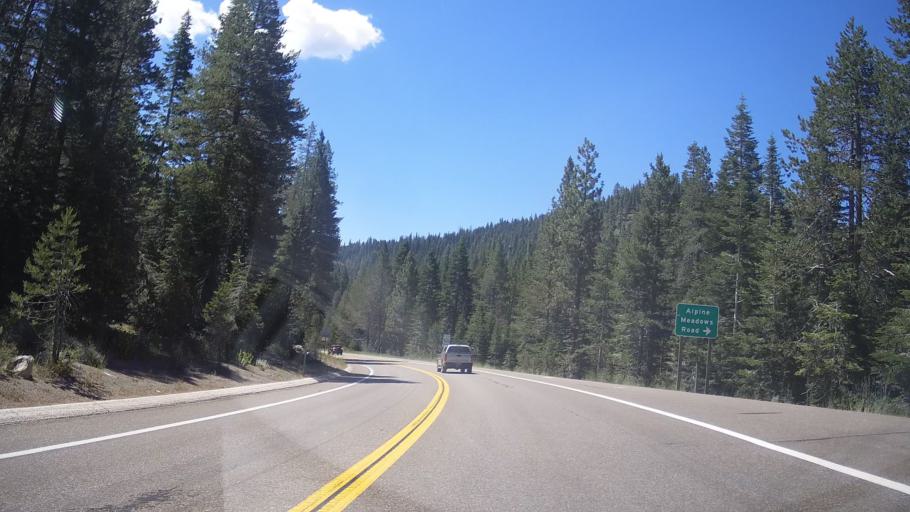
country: US
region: California
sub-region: Placer County
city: Sunnyside-Tahoe City
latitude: 39.1913
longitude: -120.1966
